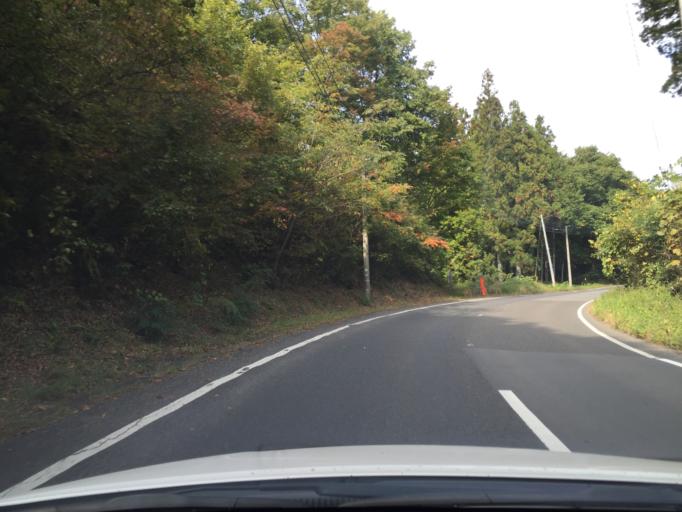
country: JP
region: Fukushima
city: Ishikawa
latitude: 36.9703
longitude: 140.4450
